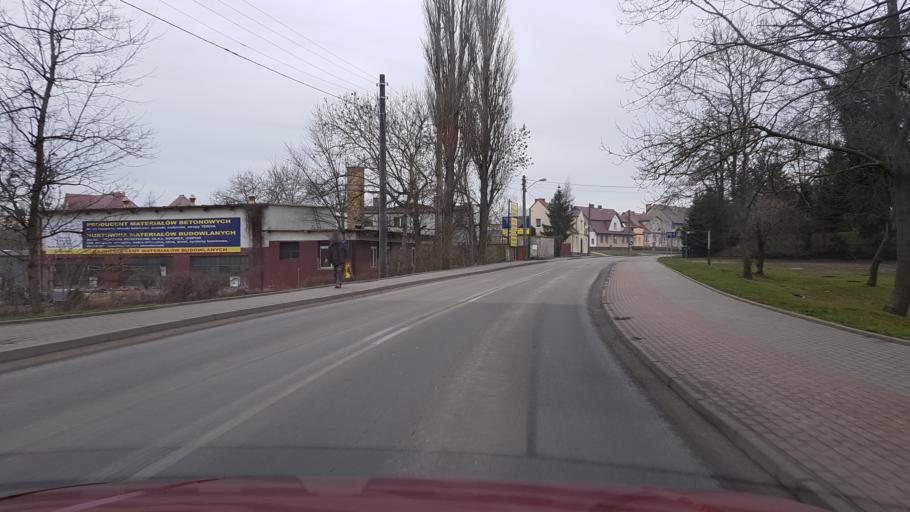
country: PL
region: West Pomeranian Voivodeship
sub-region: Powiat policki
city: Police
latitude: 53.5913
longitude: 14.5423
